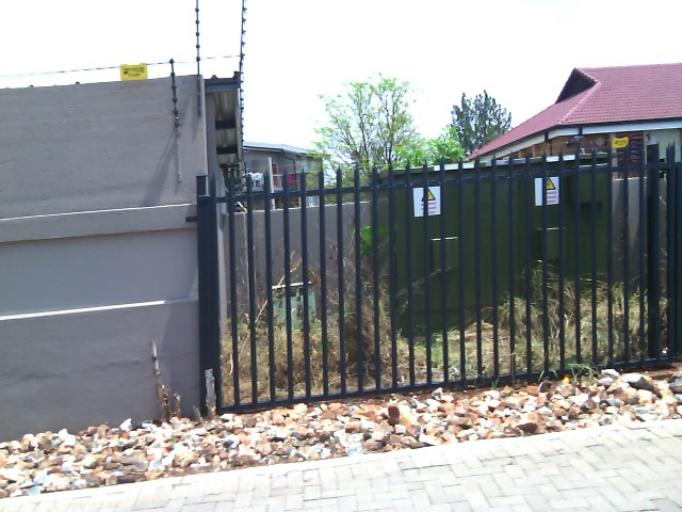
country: ZA
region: Gauteng
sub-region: City of Tshwane Metropolitan Municipality
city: Centurion
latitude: -25.8371
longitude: 28.1962
